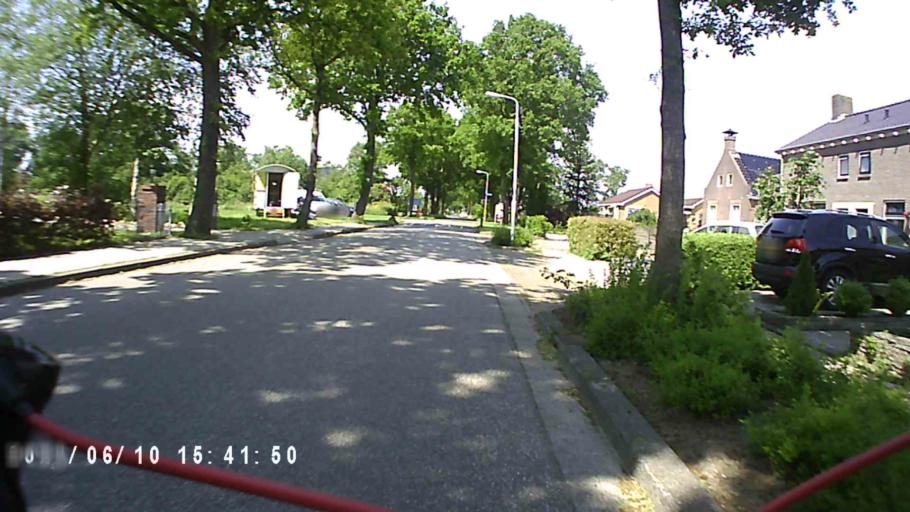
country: NL
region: Friesland
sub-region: Gemeente Achtkarspelen
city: Boelenslaan
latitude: 53.1649
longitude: 6.1445
